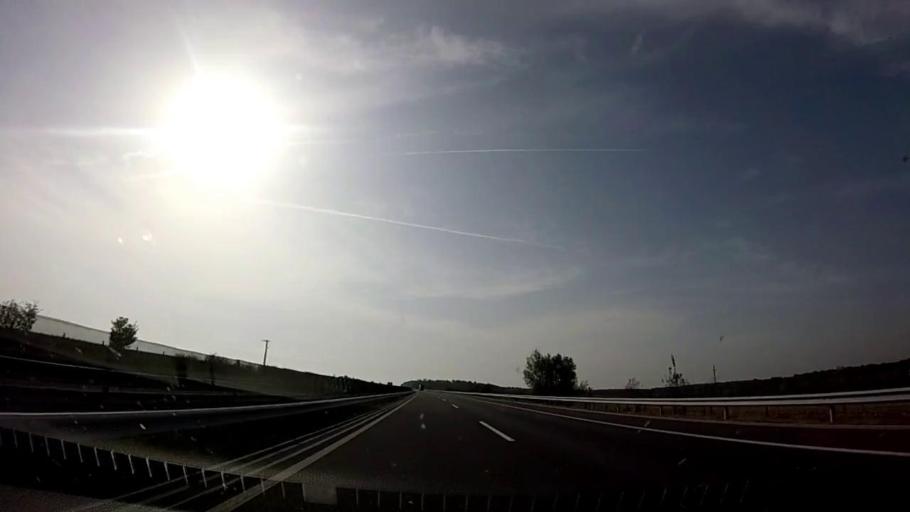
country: HU
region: Zala
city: Zalakomar
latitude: 46.5998
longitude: 17.2514
